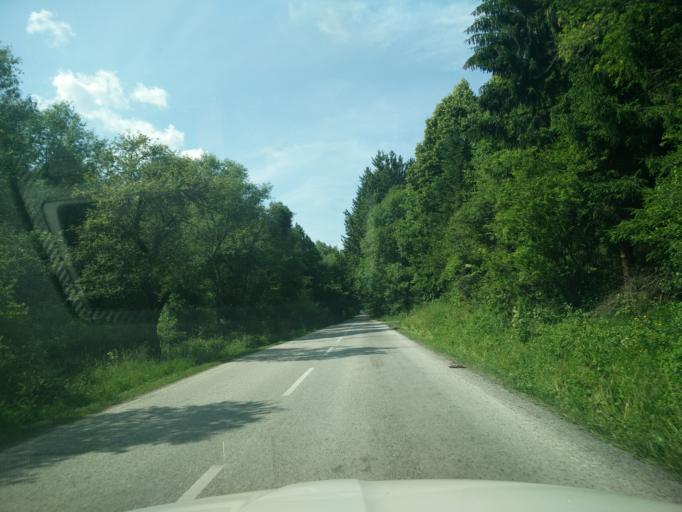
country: SK
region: Nitriansky
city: Prievidza
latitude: 48.9210
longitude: 18.6466
